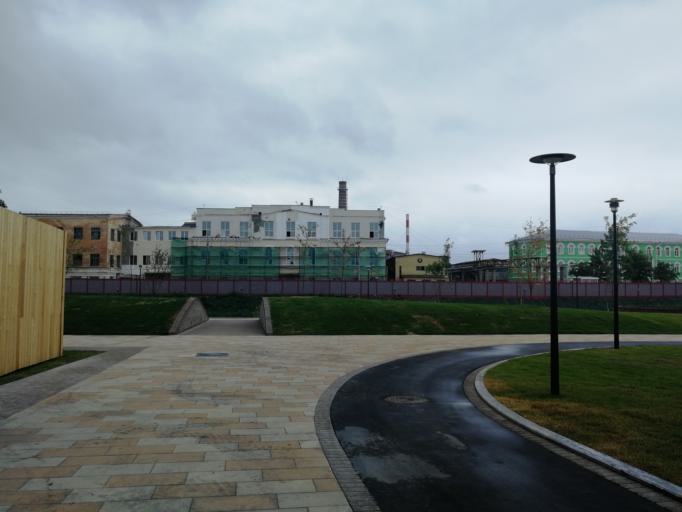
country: RU
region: Tula
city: Tula
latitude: 54.1973
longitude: 37.6187
